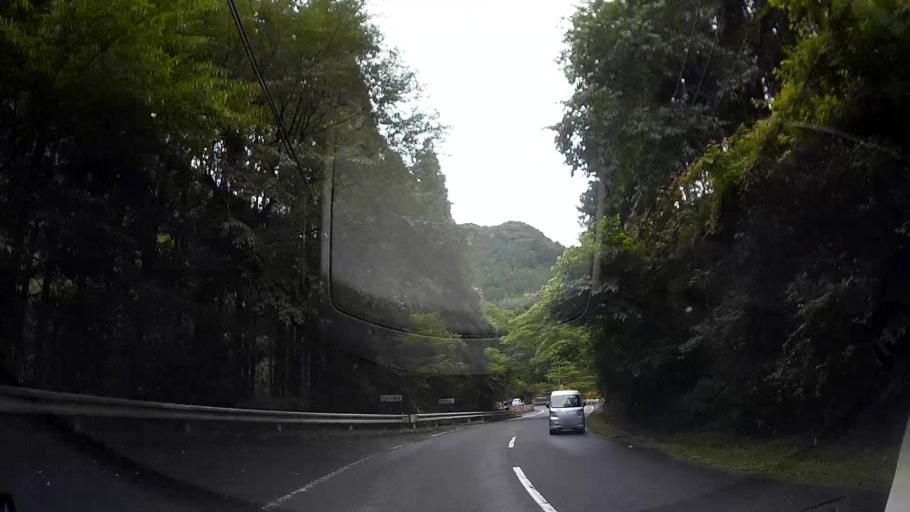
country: JP
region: Kumamoto
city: Kikuchi
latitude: 33.0735
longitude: 130.9275
